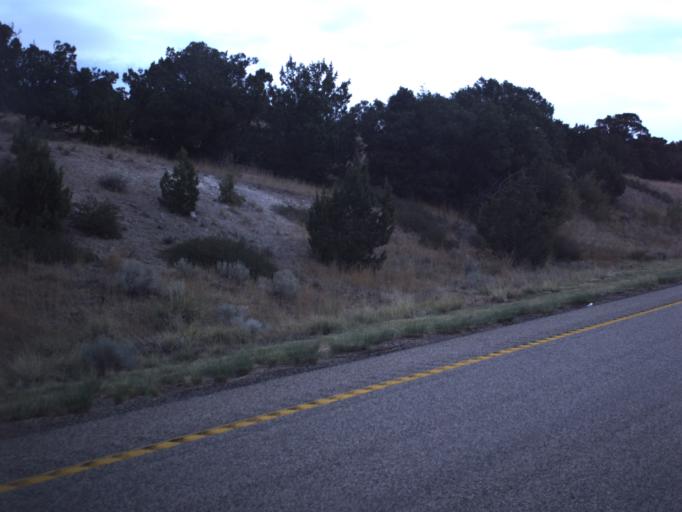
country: US
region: Utah
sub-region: Beaver County
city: Beaver
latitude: 38.6046
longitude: -112.5325
